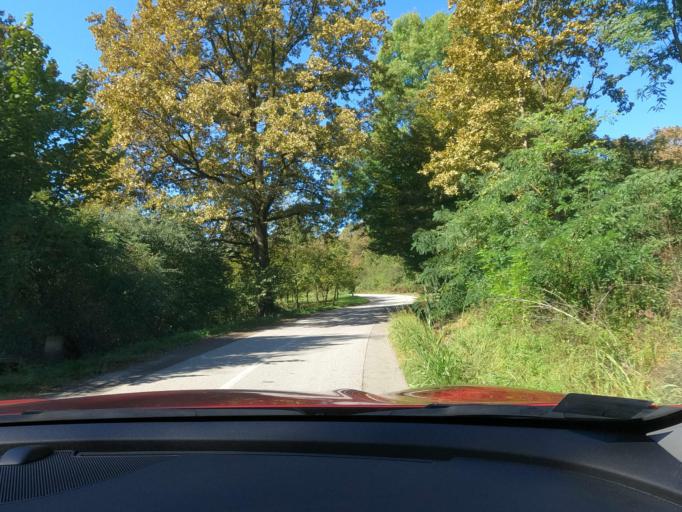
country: HR
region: Sisacko-Moslavacka
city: Petrinja
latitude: 45.4680
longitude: 16.2989
